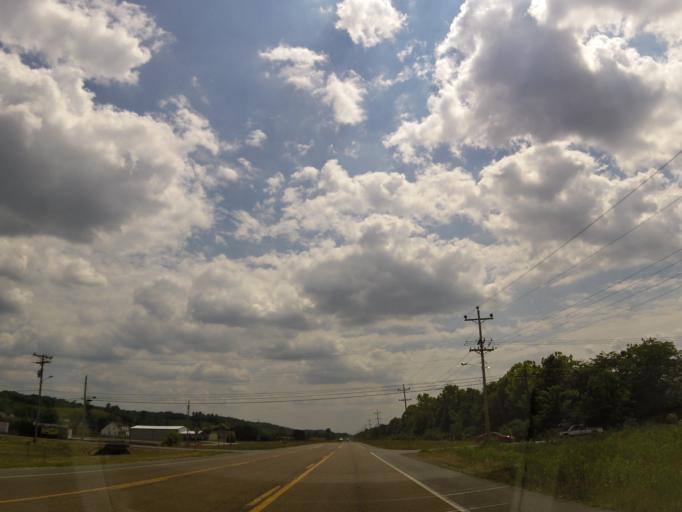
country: US
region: Tennessee
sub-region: Sequatchie County
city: Dunlap
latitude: 35.3390
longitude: -85.4137
